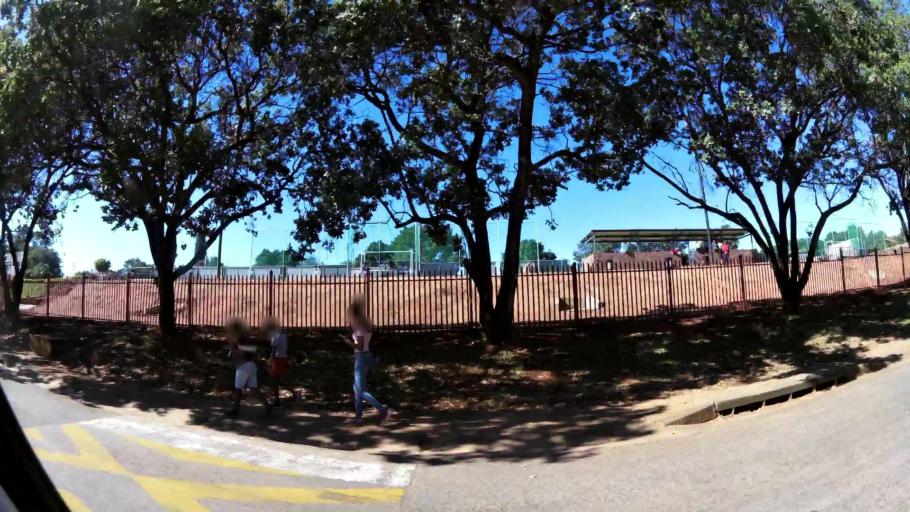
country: ZA
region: Limpopo
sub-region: Mopani District Municipality
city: Tzaneen
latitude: -23.8369
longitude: 30.1498
